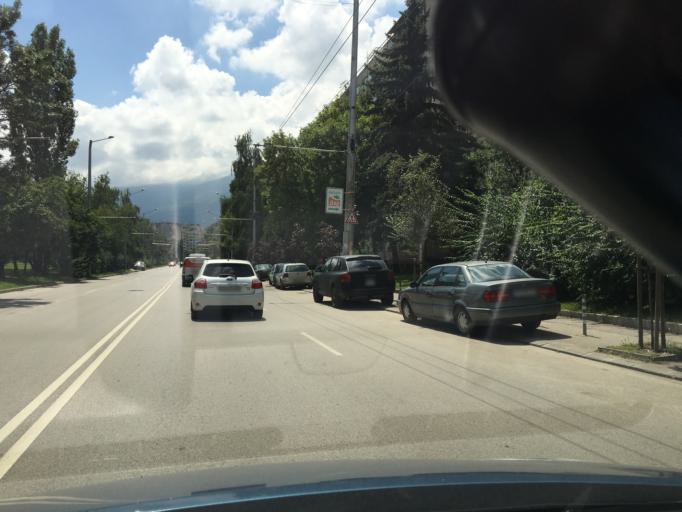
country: BG
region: Sofia-Capital
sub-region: Stolichna Obshtina
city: Sofia
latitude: 42.6688
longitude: 23.3036
